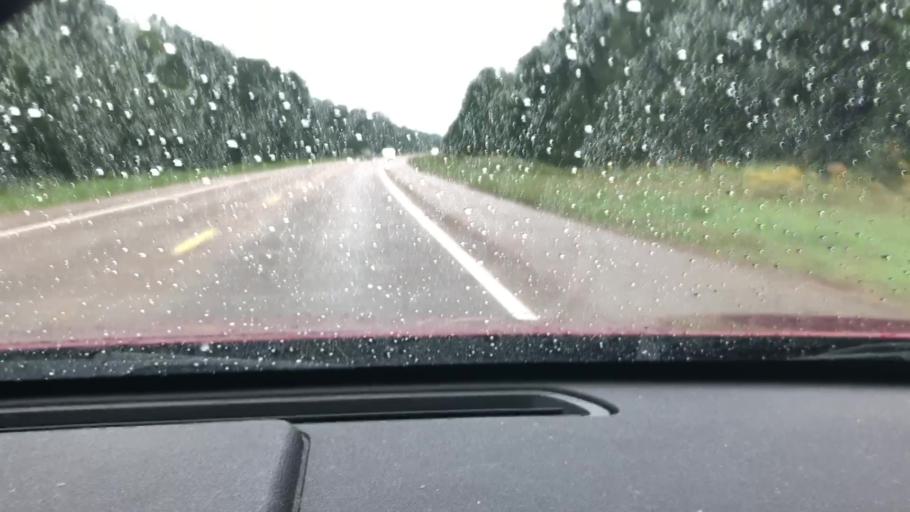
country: US
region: Arkansas
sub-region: Columbia County
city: Magnolia
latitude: 33.2987
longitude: -93.2636
